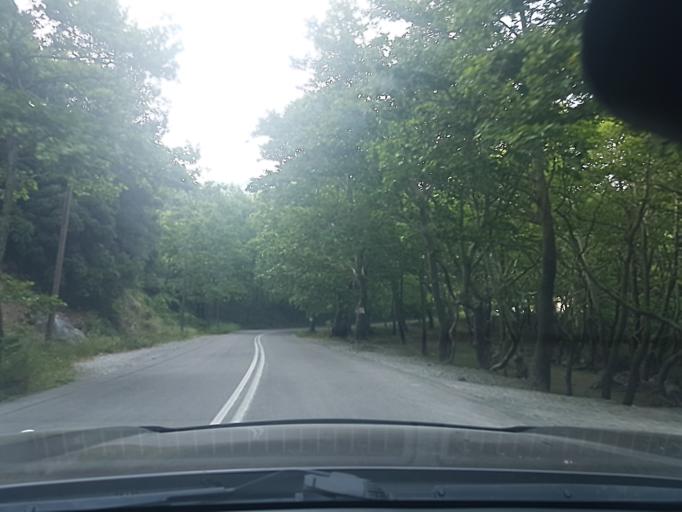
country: GR
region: Central Greece
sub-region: Nomos Evvoias
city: Yimnon
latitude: 38.5870
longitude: 23.8453
